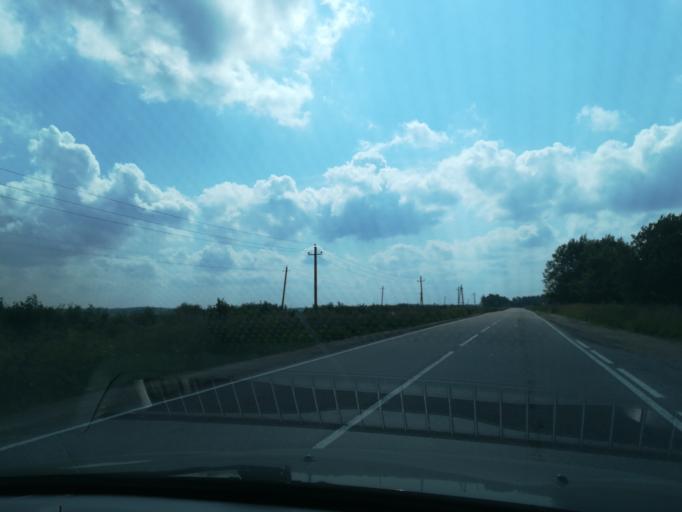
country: RU
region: Leningrad
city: Kopor'ye
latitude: 59.7019
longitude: 29.0553
